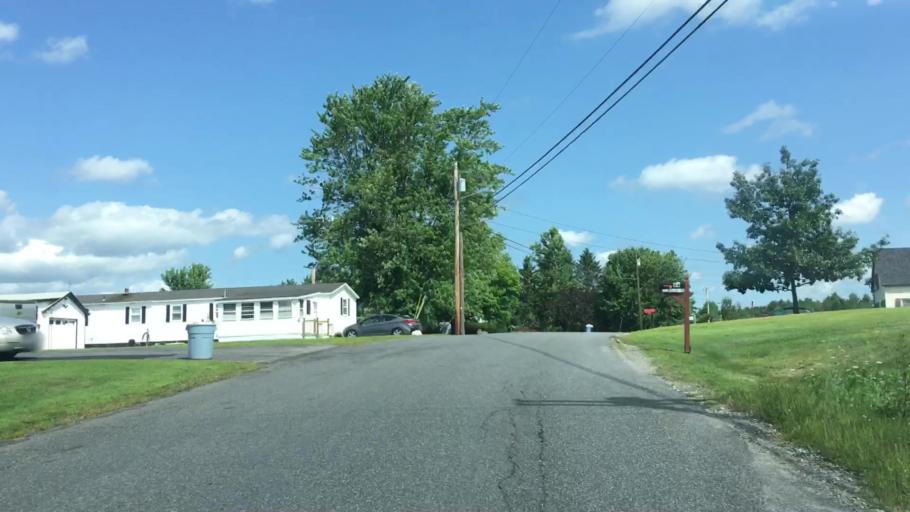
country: US
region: Maine
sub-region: Kennebec County
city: Manchester
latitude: 44.3613
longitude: -69.8160
